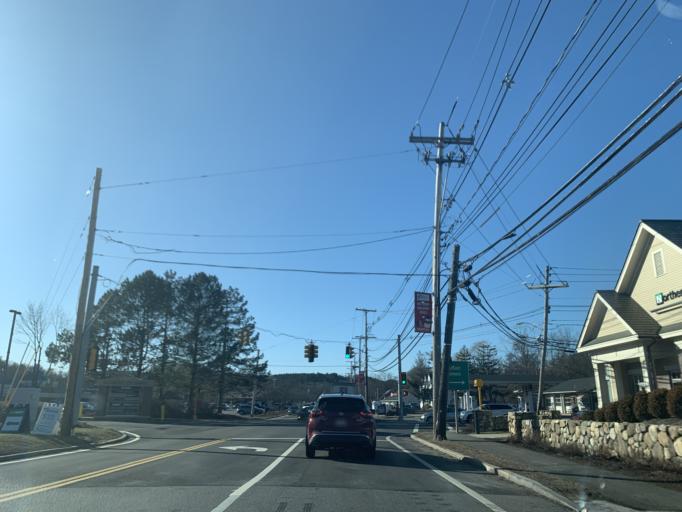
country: US
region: Massachusetts
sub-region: Middlesex County
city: Sudbury
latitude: 42.3609
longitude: -71.4216
